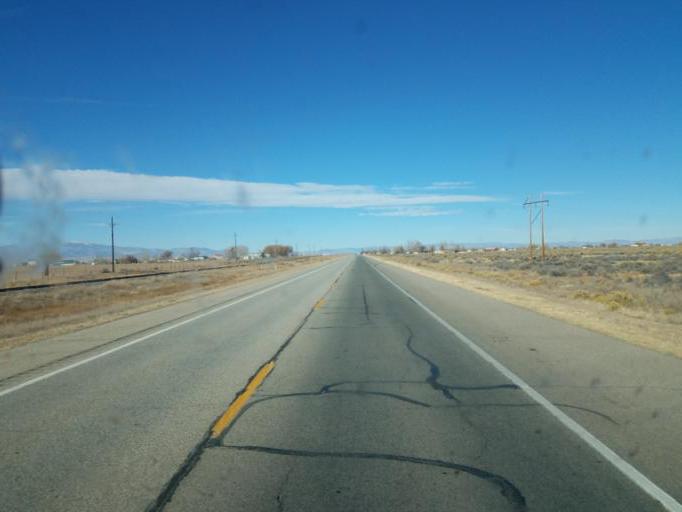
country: US
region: Colorado
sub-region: Alamosa County
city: Alamosa
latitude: 37.4996
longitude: -105.9521
